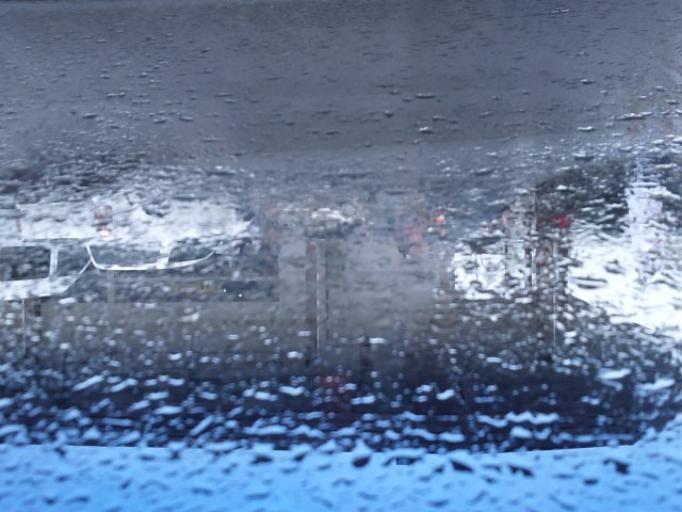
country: BR
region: Santa Catarina
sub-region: Joinville
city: Joinville
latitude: -26.0655
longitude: -48.8597
